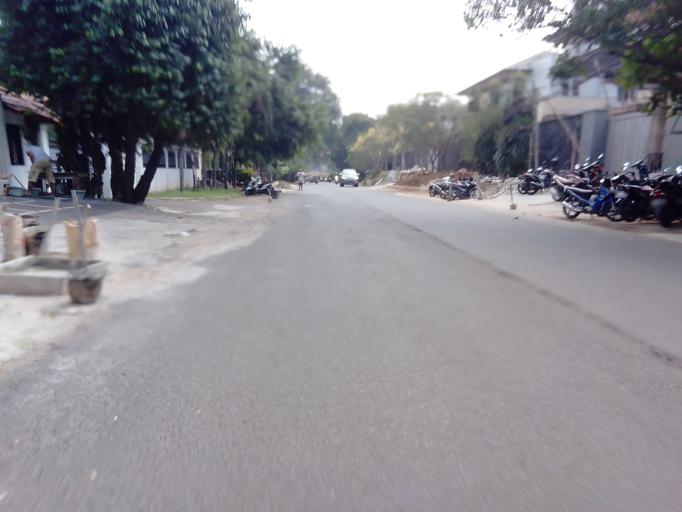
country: ID
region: Jakarta Raya
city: Jakarta
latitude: -6.2250
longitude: 106.7928
